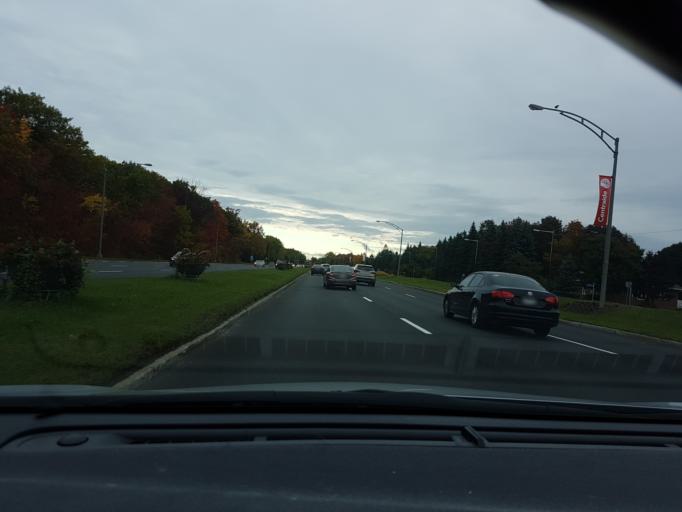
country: CA
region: Quebec
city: Quebec
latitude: 46.7768
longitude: -71.2696
